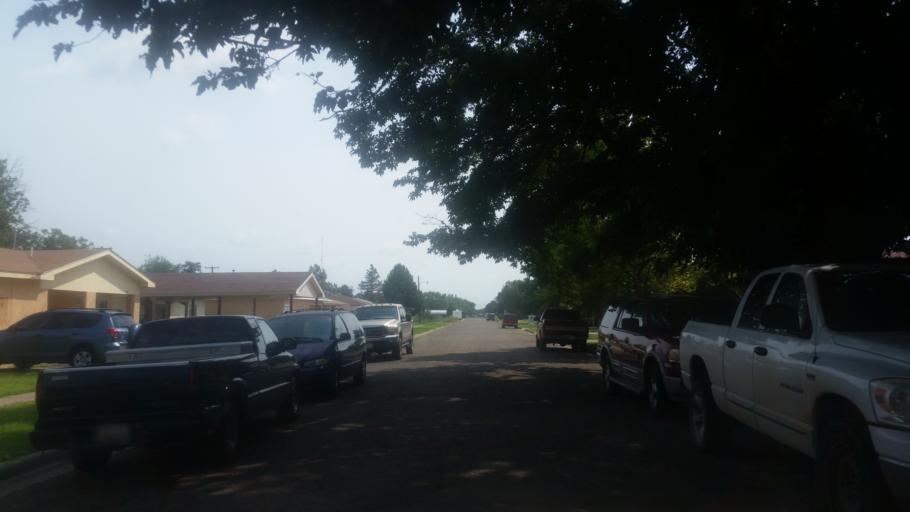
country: US
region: New Mexico
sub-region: Curry County
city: Clovis
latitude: 34.4292
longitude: -103.2114
